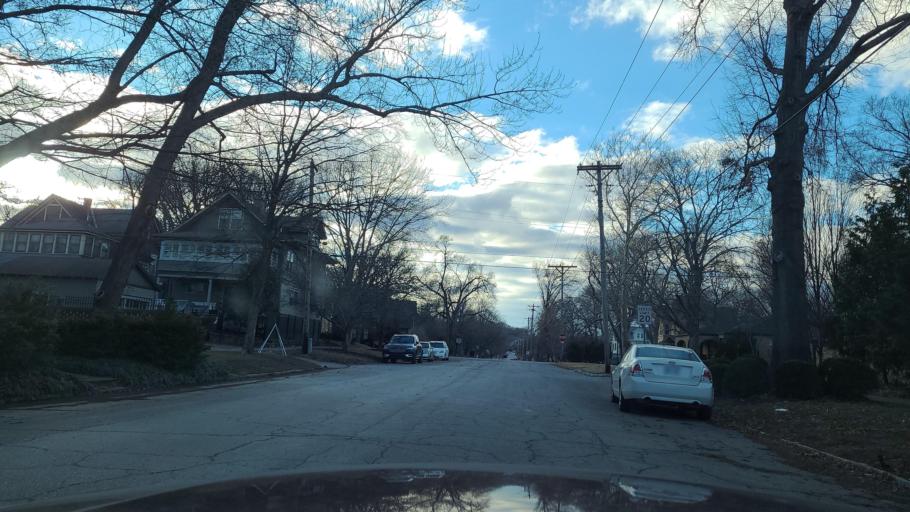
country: US
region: Kansas
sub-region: Douglas County
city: Lawrence
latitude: 38.9713
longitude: -95.2420
